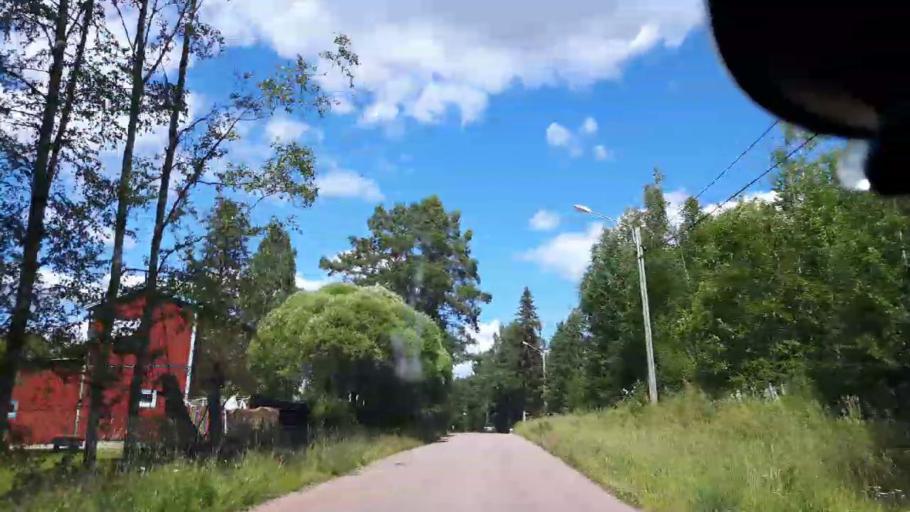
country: SE
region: Jaemtland
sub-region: Ragunda Kommun
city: Hammarstrand
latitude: 62.9504
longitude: 16.6876
